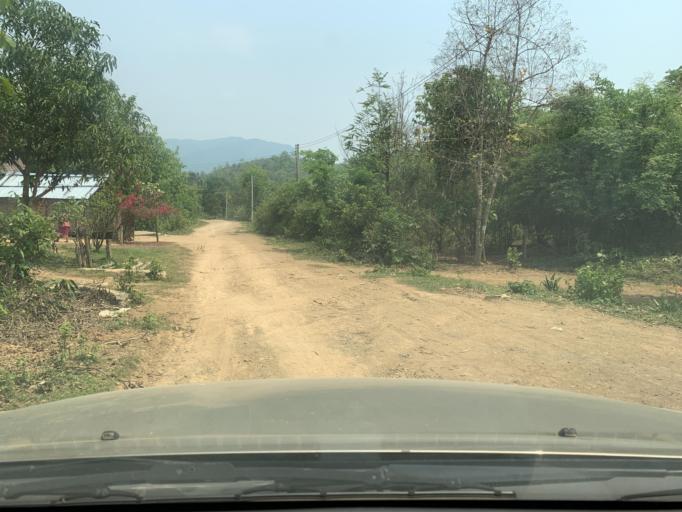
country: LA
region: Louangphabang
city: Louangphabang
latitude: 19.9445
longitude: 102.1339
